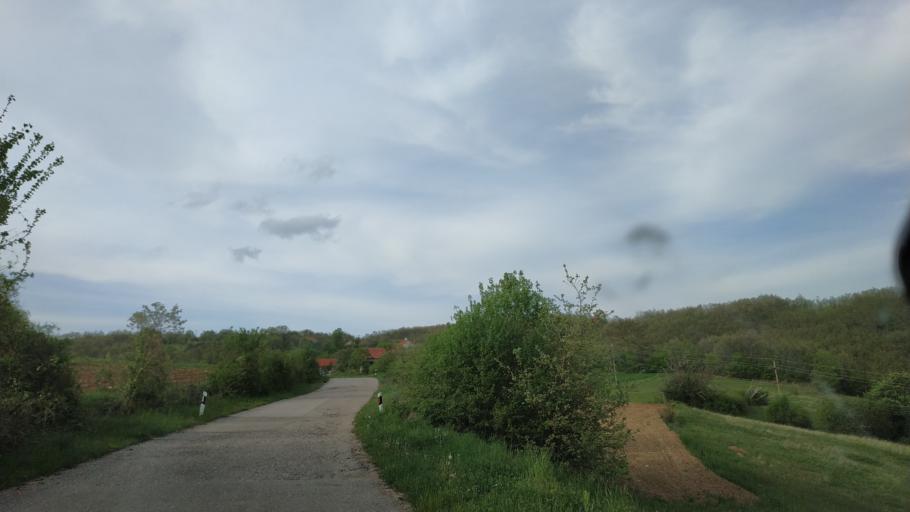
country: RS
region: Central Serbia
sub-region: Zajecarski Okrug
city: Soko Banja
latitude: 43.5359
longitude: 21.8785
